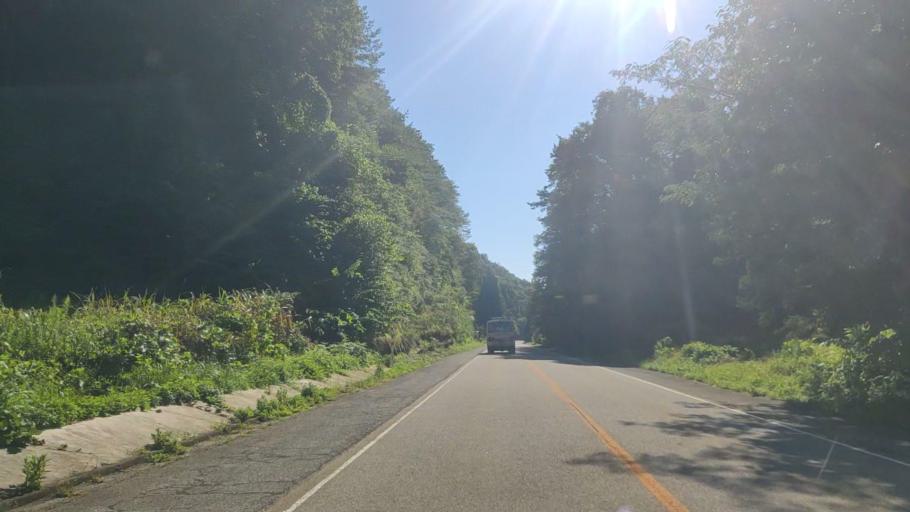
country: JP
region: Ishikawa
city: Nanao
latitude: 37.2462
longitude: 136.9926
